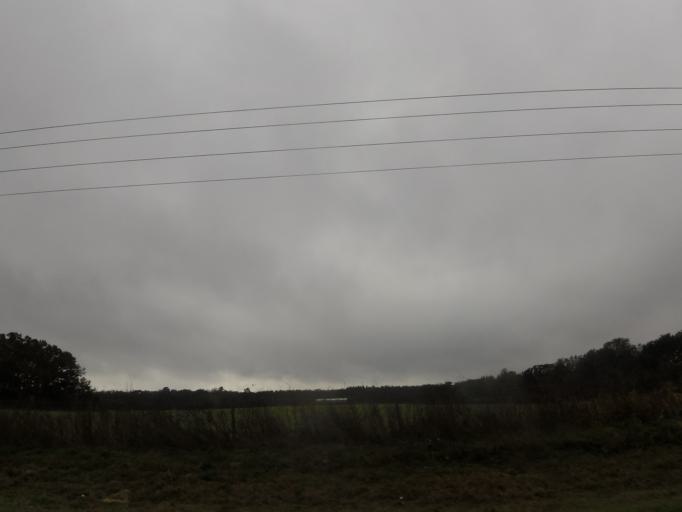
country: US
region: Florida
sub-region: Gilchrist County
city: Trenton
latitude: 29.8025
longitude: -82.9452
